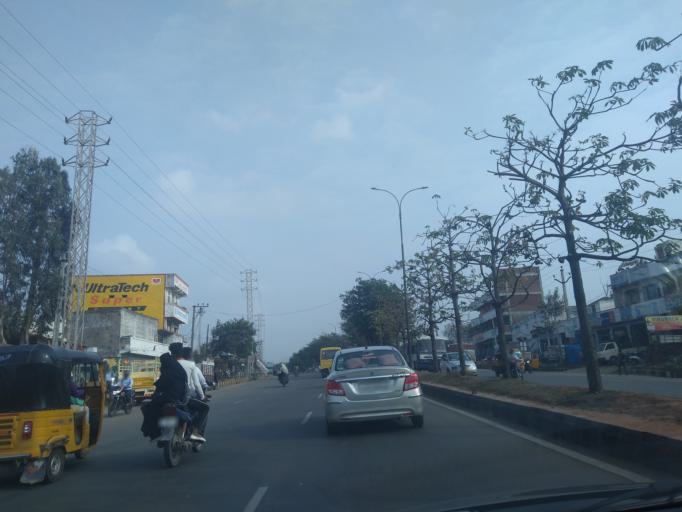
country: IN
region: Telangana
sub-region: Rangareddi
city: Balapur
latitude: 17.3197
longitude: 78.4349
